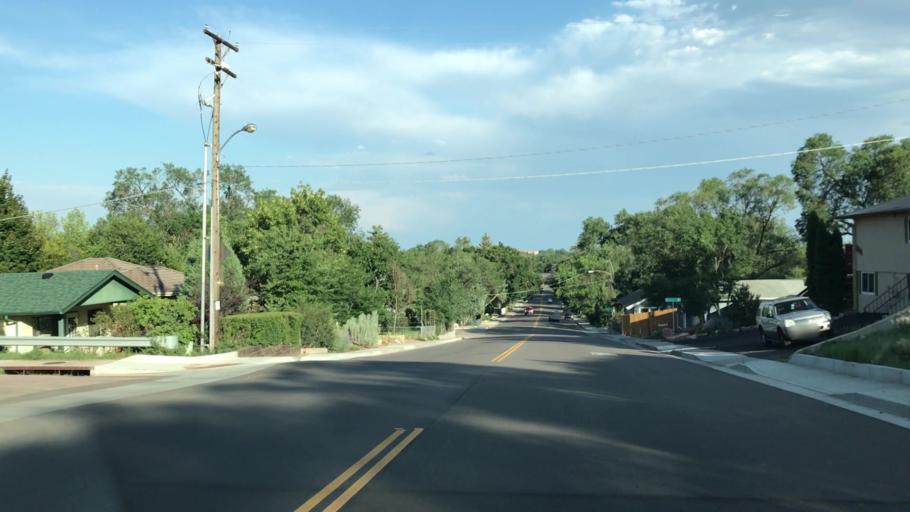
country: US
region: Colorado
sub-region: El Paso County
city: Colorado Springs
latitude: 38.8512
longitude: -104.8602
